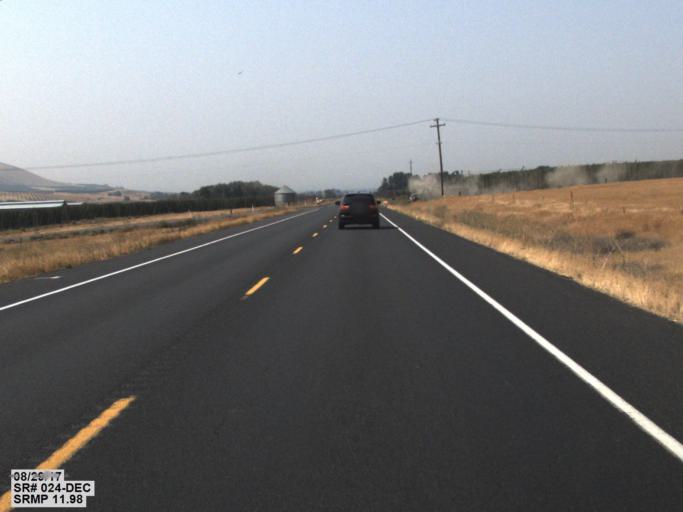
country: US
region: Washington
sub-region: Yakima County
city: Zillah
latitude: 46.5245
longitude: -120.2489
